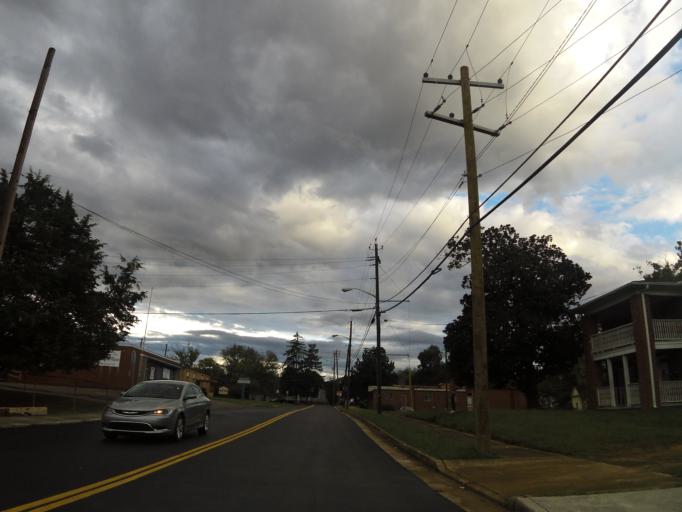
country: US
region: Tennessee
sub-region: Knox County
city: Knoxville
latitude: 35.9978
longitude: -83.8790
